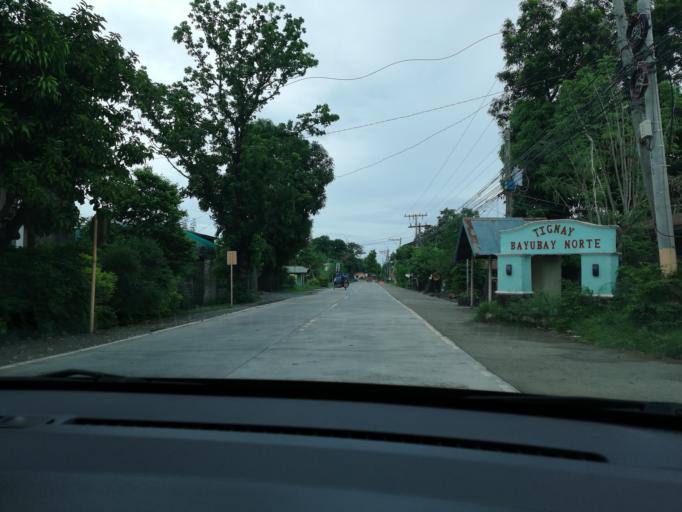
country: PH
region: Ilocos
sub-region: Province of Ilocos Sur
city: Bantay
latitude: 17.5843
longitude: 120.3826
